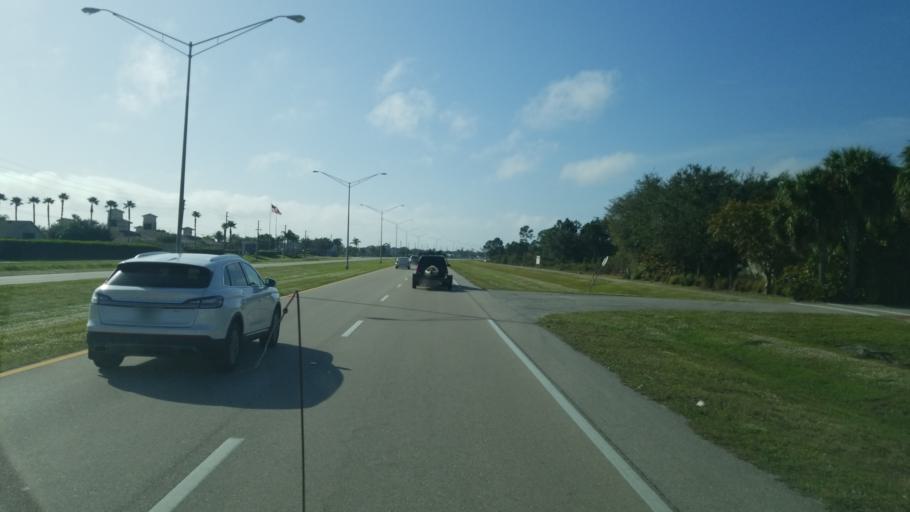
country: US
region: Florida
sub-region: Charlotte County
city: Port Charlotte
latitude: 27.0095
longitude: -82.0540
